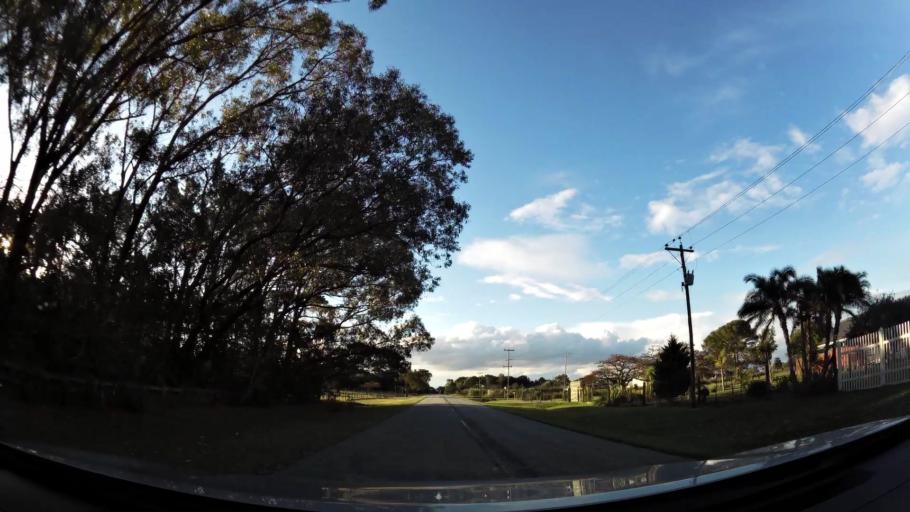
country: ZA
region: Eastern Cape
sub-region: Nelson Mandela Bay Metropolitan Municipality
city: Port Elizabeth
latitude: -33.9805
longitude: 25.4839
